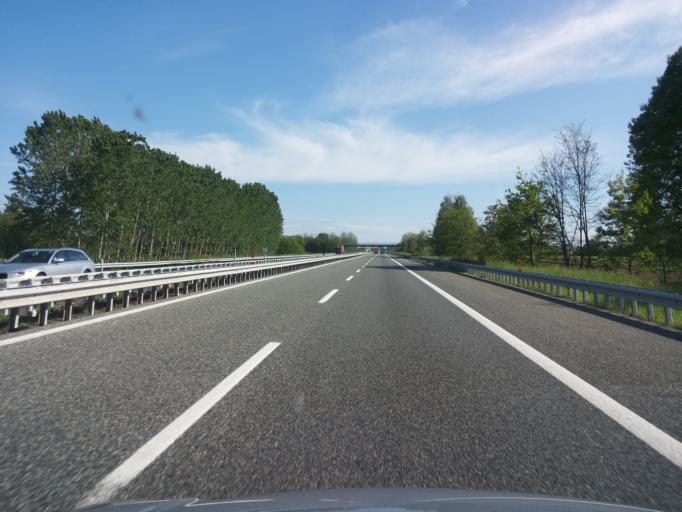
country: IT
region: Piedmont
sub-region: Provincia di Novara
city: Carpignano Sesia
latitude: 45.5502
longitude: 8.4228
